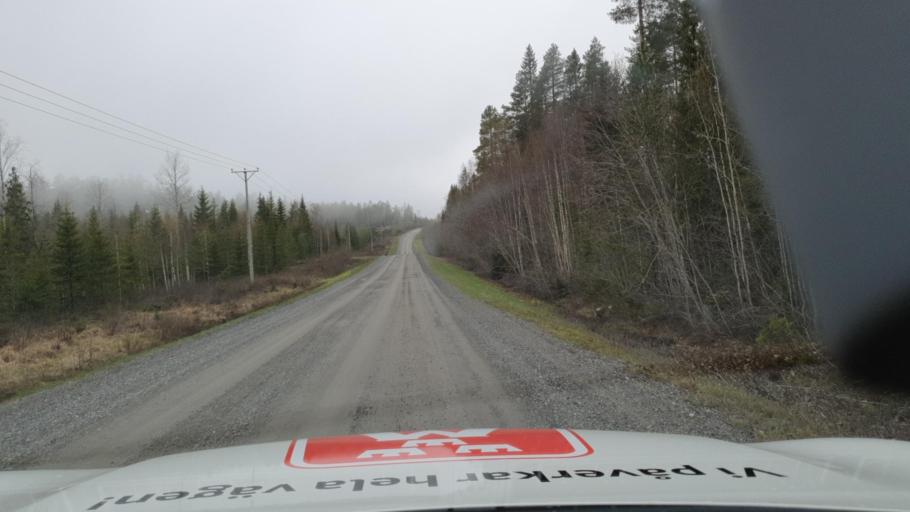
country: SE
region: Vaesterbotten
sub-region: Nordmalings Kommun
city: Nordmaling
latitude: 63.7655
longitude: 19.4684
